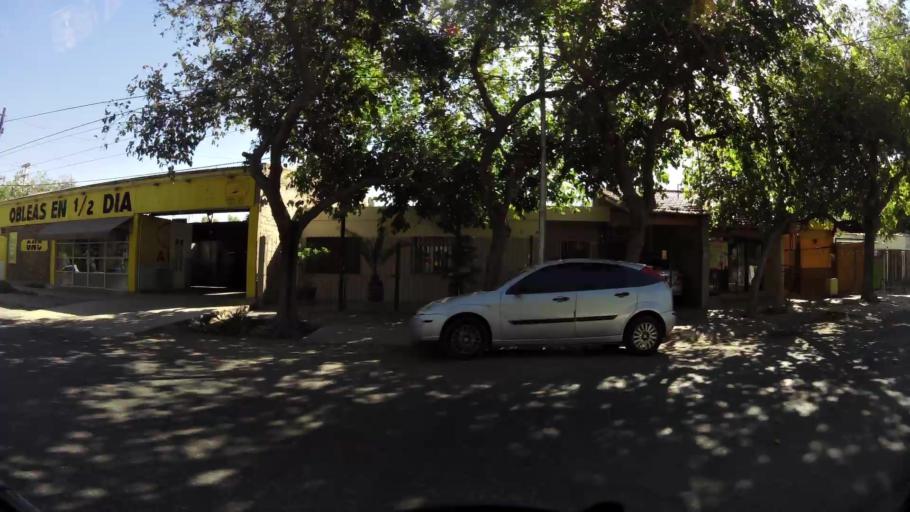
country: AR
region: San Juan
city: San Juan
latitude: -31.5226
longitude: -68.5366
